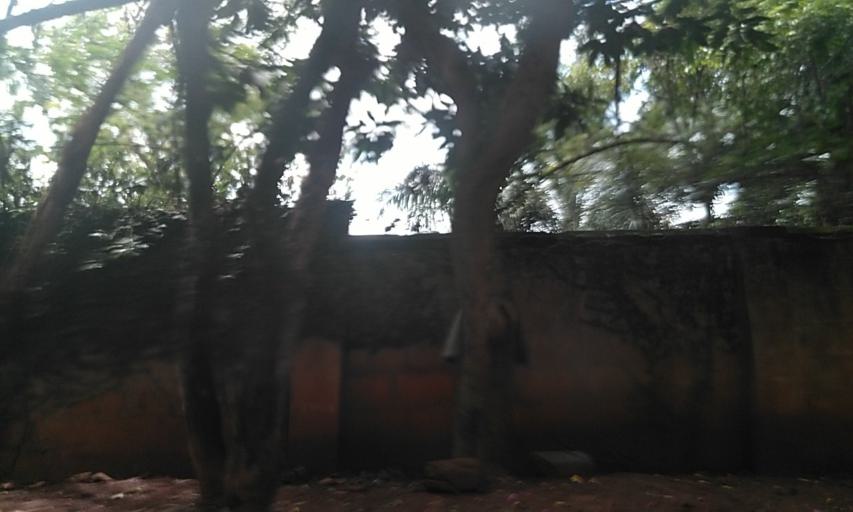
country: UG
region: Central Region
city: Kampala Central Division
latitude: 0.3324
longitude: 32.5881
